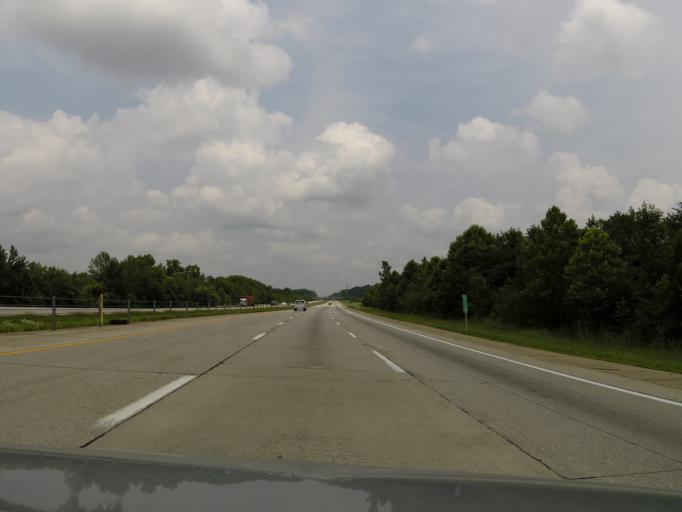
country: US
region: Kentucky
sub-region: Bullitt County
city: Lebanon Junction
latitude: 37.8984
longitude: -85.6981
